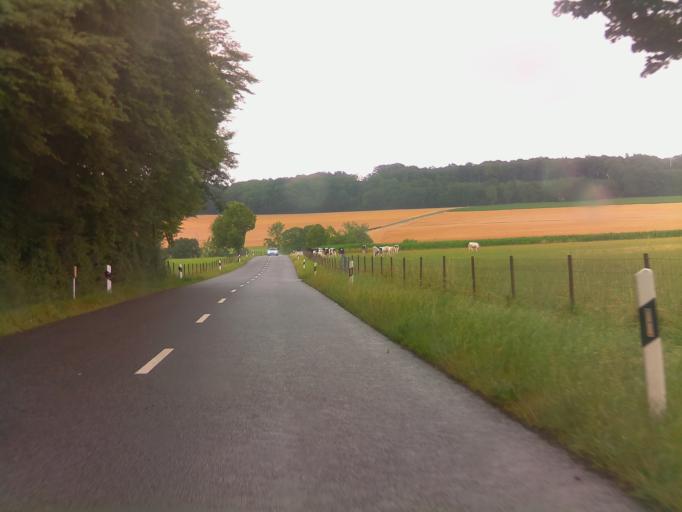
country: LU
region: Grevenmacher
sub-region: Canton de Remich
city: Mondorf-les-Bains
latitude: 49.5229
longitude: 6.2800
